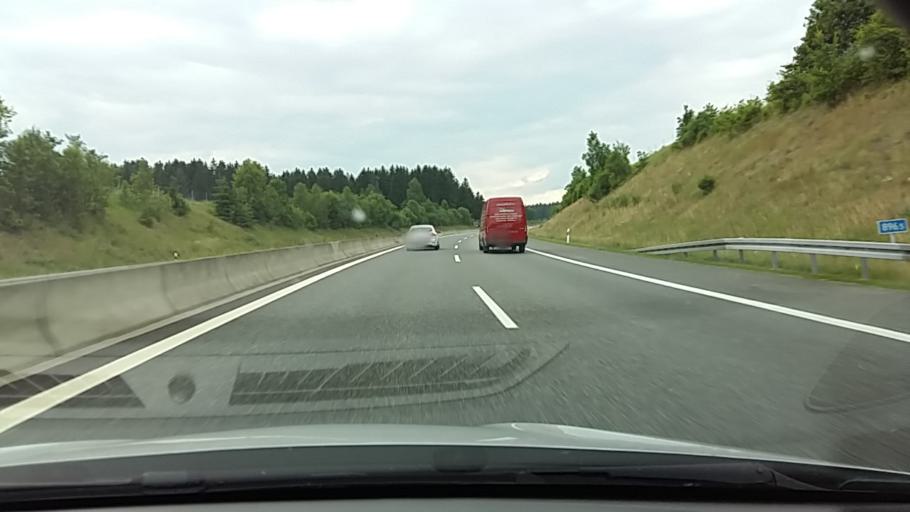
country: DE
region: Bavaria
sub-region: Upper Palatinate
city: Moosbach
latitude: 49.6129
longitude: 12.3802
